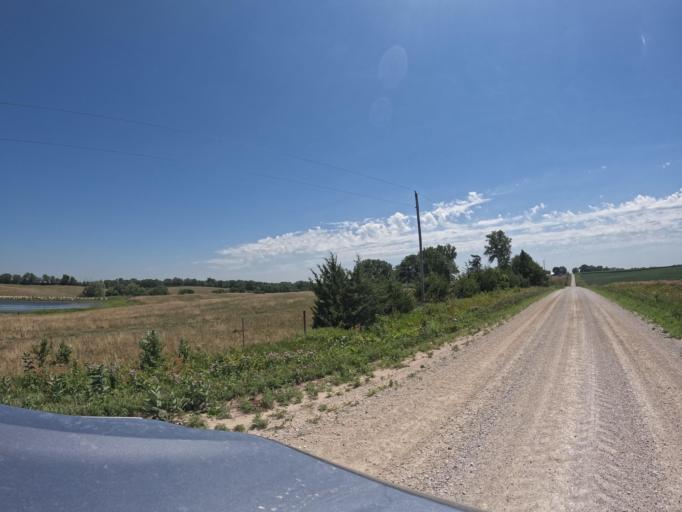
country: US
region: Iowa
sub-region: Keokuk County
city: Sigourney
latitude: 41.4217
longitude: -92.3164
